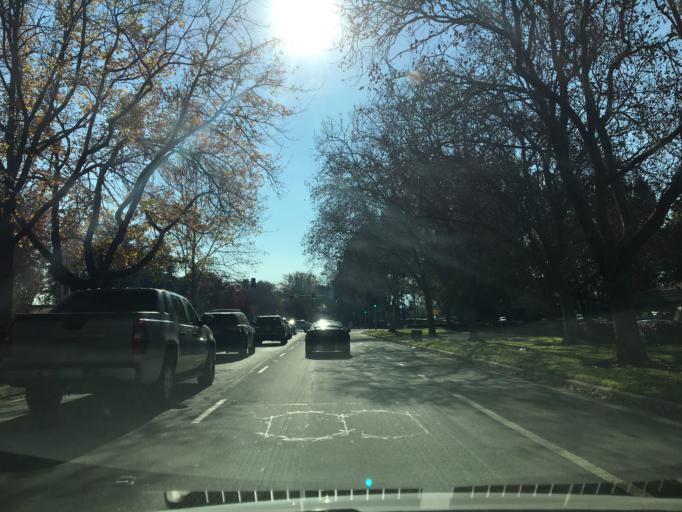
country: US
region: California
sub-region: Santa Clara County
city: Milpitas
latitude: 37.3981
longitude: -121.8911
